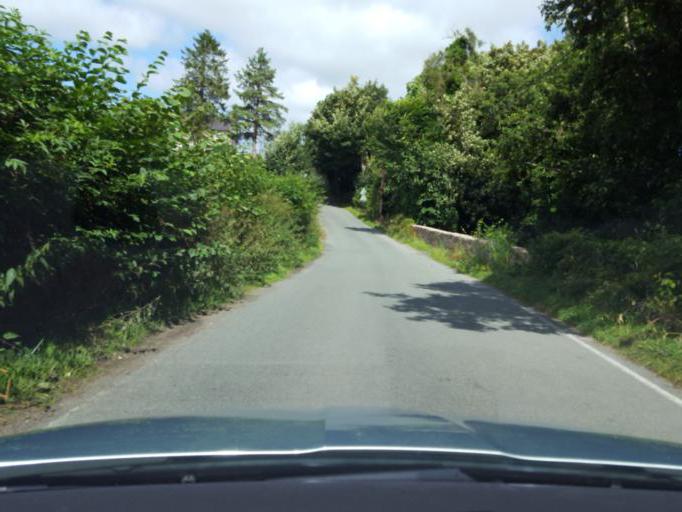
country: GB
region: Wales
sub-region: County of Flintshire
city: Leeswood
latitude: 53.1236
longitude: -3.1366
